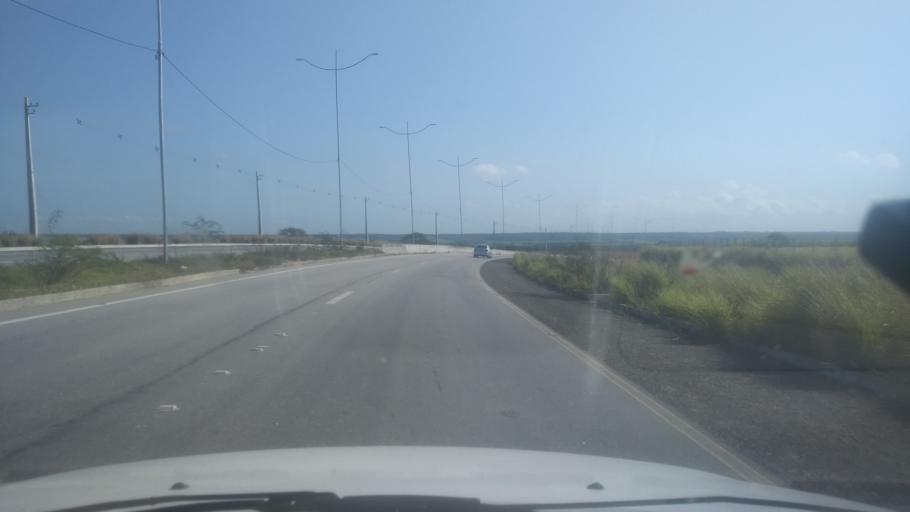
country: BR
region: Rio Grande do Norte
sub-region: Macaiba
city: Macaiba
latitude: -5.8262
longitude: -35.3699
